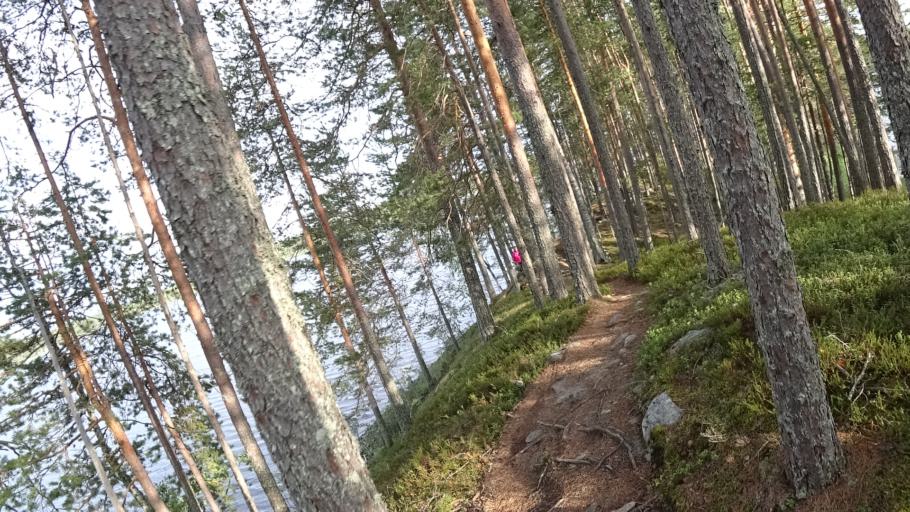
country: FI
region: North Karelia
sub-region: Joensuu
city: Ilomantsi
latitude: 62.5675
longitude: 31.1819
